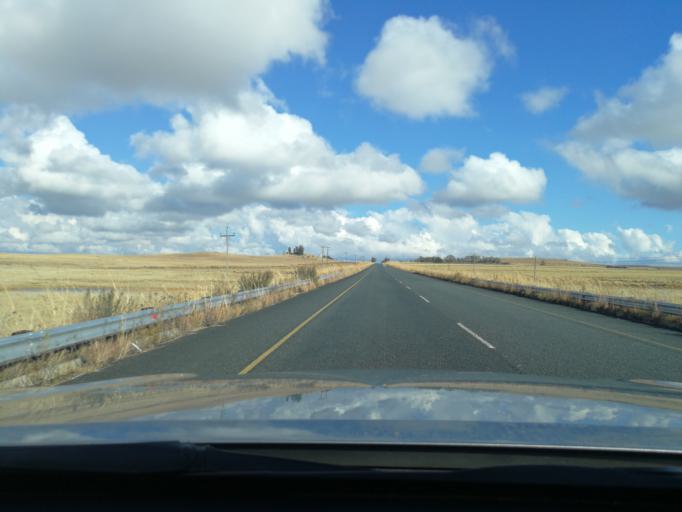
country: ZA
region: Orange Free State
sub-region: Thabo Mofutsanyana District Municipality
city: Reitz
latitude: -27.9889
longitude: 28.3748
